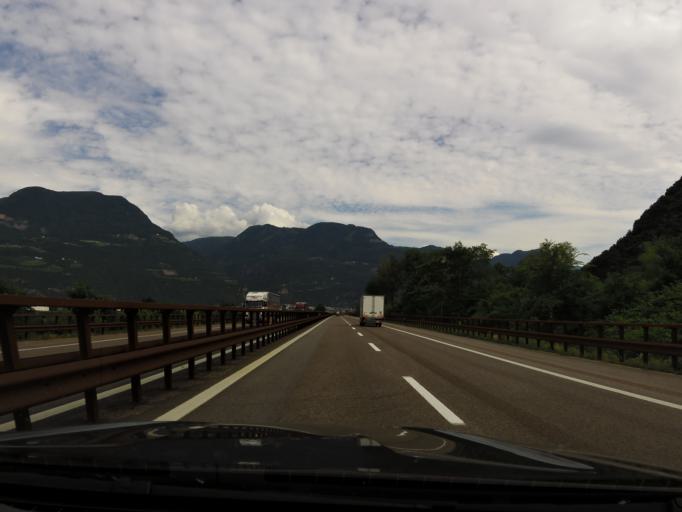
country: IT
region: Trentino-Alto Adige
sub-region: Bolzano
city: San Giacomo
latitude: 46.4472
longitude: 11.3114
